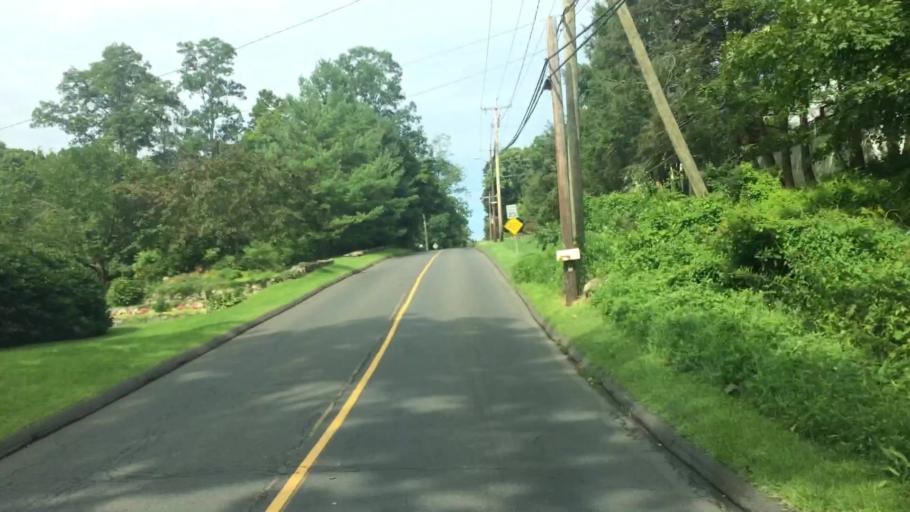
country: US
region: Connecticut
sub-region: Fairfield County
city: Danbury
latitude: 41.4054
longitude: -73.4934
